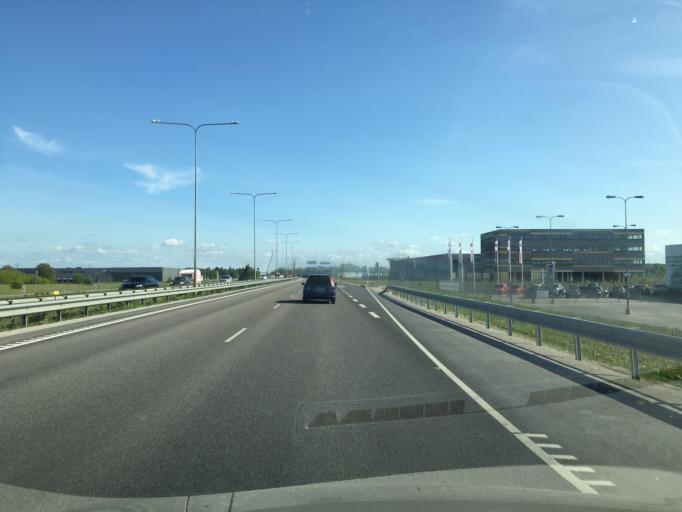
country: EE
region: Harju
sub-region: Rae vald
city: Jueri
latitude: 59.3840
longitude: 24.8355
